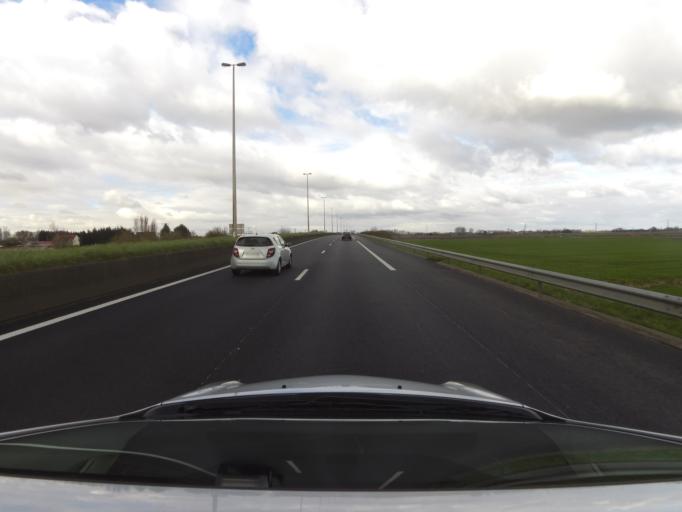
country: FR
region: Nord-Pas-de-Calais
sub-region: Departement du Pas-de-Calais
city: Vieille-Eglise
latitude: 50.9327
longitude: 2.0339
